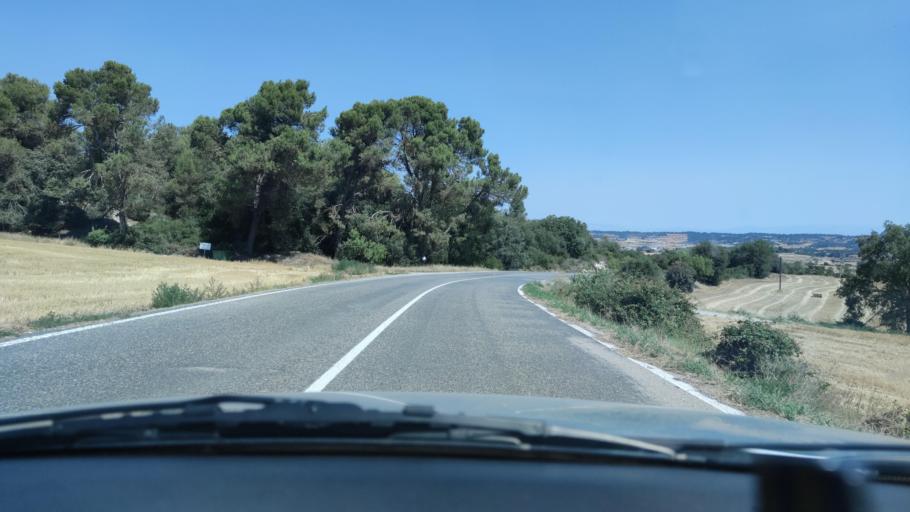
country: ES
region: Catalonia
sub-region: Provincia de Tarragona
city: Santa Coloma de Queralt
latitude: 41.6010
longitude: 1.3480
